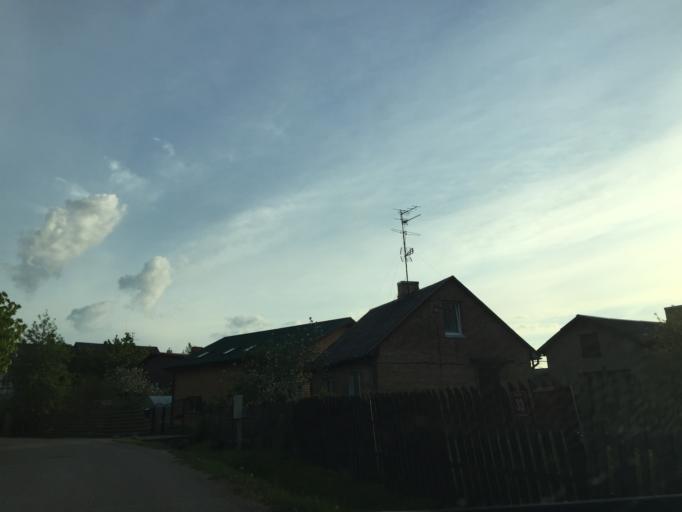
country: LV
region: Ozolnieku
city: Ozolnieki
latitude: 56.6558
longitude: 23.7676
